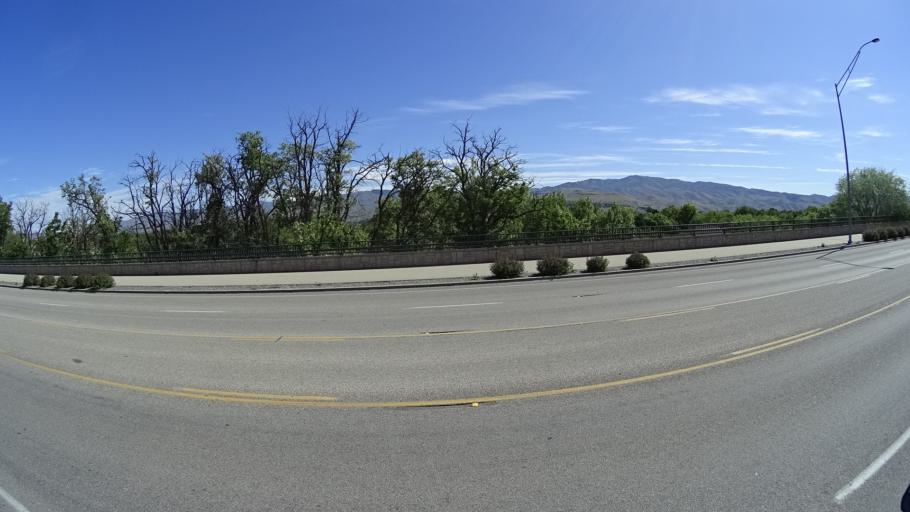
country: US
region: Idaho
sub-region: Ada County
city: Boise
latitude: 43.5696
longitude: -116.1853
